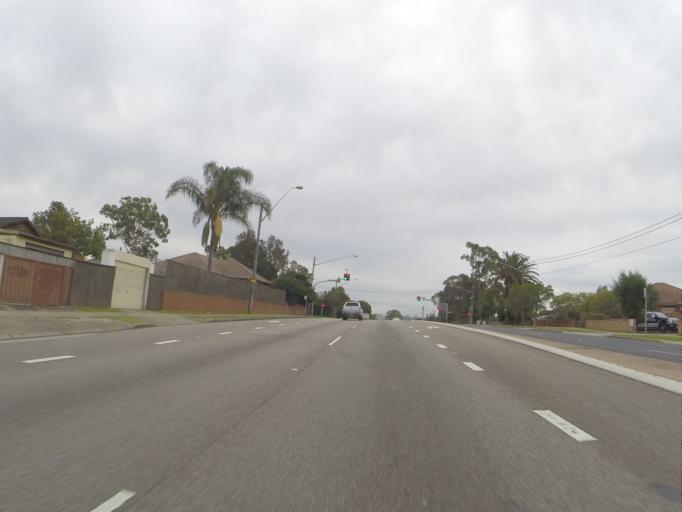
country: AU
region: New South Wales
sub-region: Bankstown
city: Padstow
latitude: -33.9543
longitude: 151.0381
